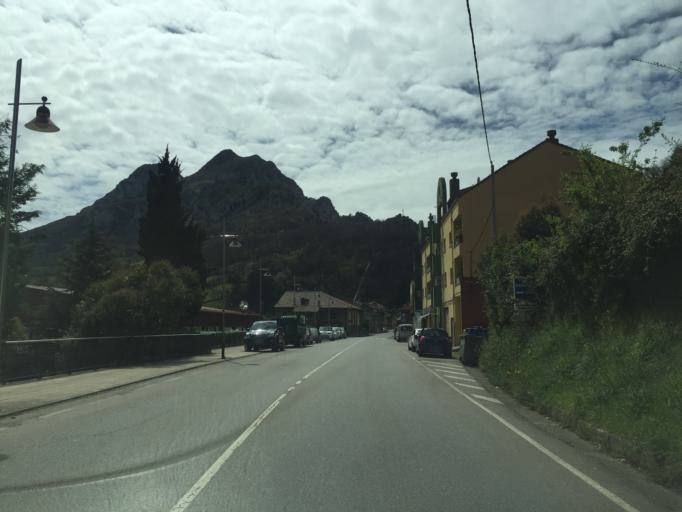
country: ES
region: Asturias
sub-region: Province of Asturias
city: Proaza
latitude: 43.2539
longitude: -6.0145
